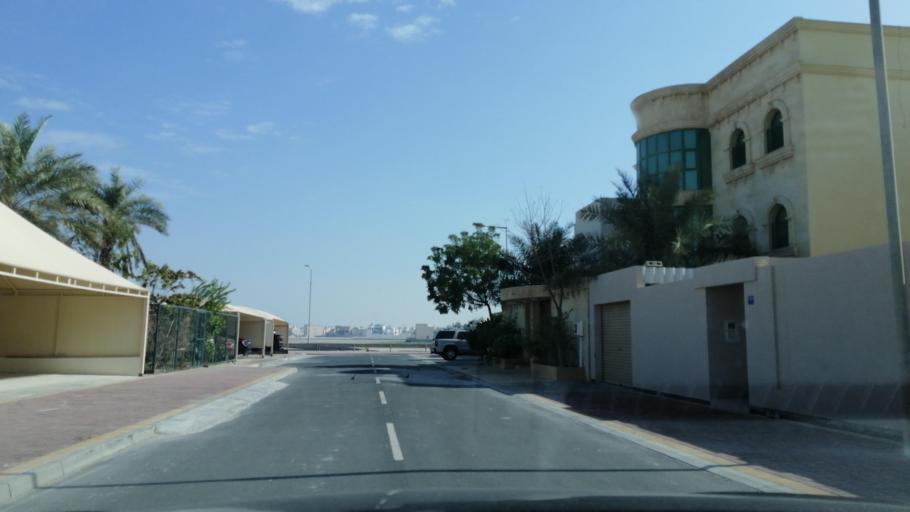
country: BH
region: Muharraq
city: Al Hadd
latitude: 26.2422
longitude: 50.6338
